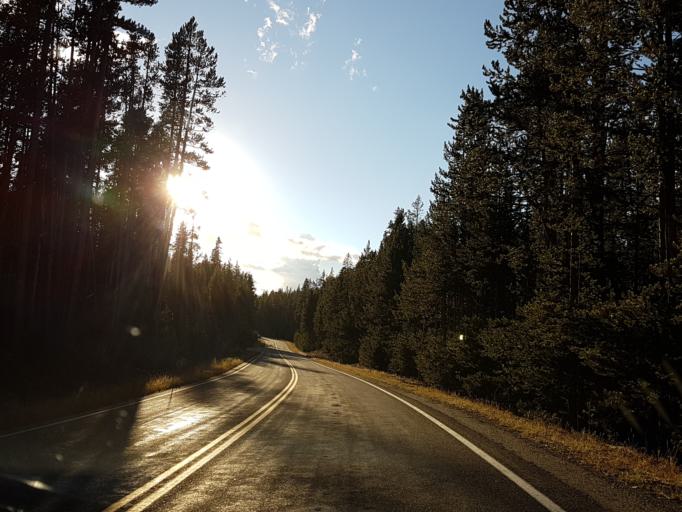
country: US
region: Montana
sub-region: Gallatin County
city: West Yellowstone
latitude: 44.4317
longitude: -110.7577
